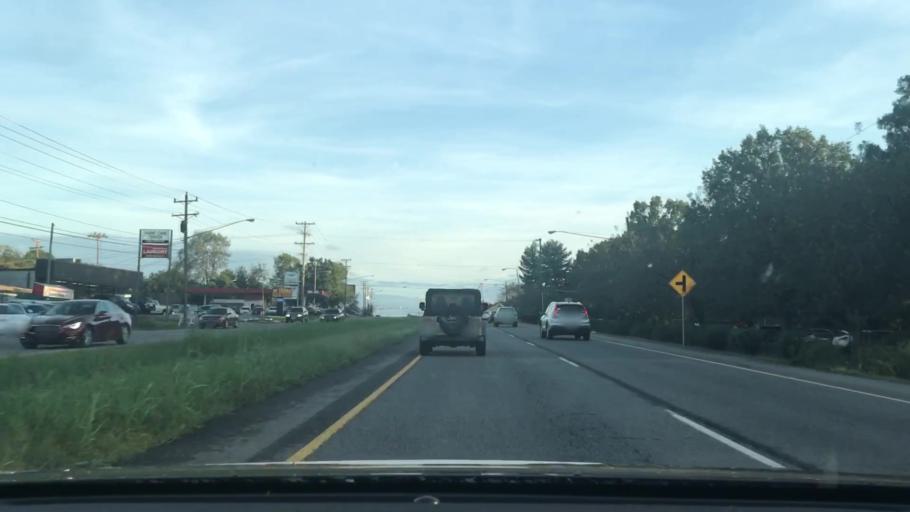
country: US
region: Tennessee
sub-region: Williamson County
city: Brentwood Estates
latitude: 36.0572
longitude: -86.7160
